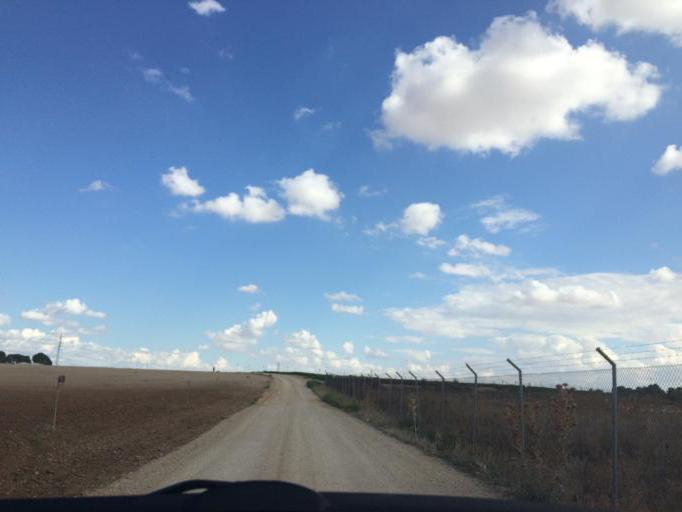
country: ES
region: Castille-La Mancha
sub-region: Provincia de Albacete
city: Albacete
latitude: 38.9588
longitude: -1.8749
